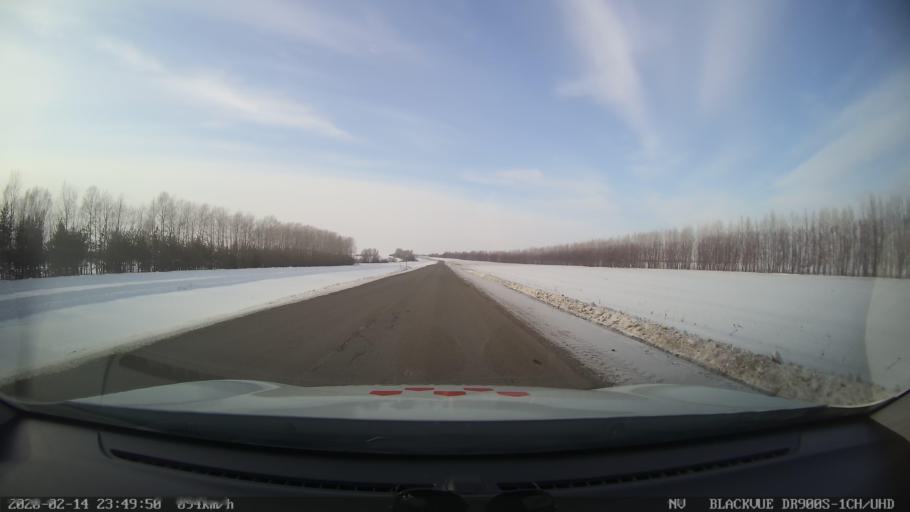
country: RU
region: Tatarstan
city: Kuybyshevskiy Zaton
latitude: 55.2561
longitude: 49.1730
